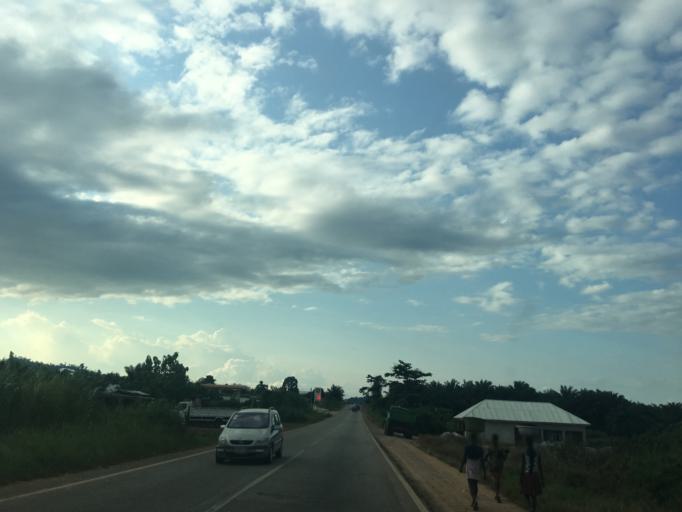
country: GH
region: Western
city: Bibiani
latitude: 6.4262
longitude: -2.3055
